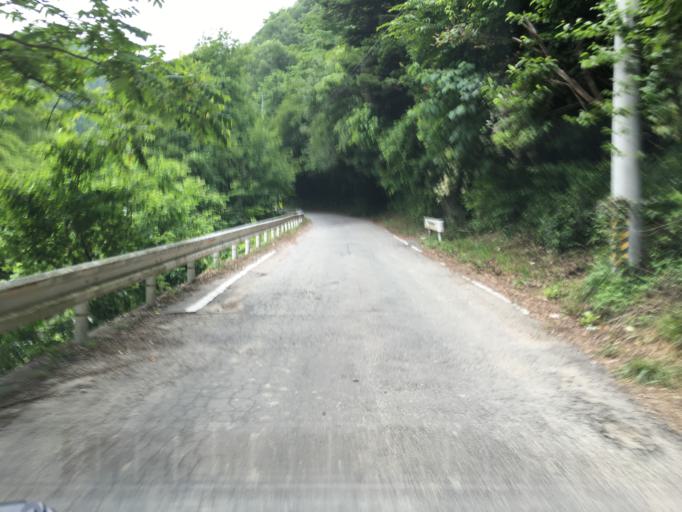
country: JP
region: Miyagi
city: Marumori
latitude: 37.7920
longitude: 140.7830
